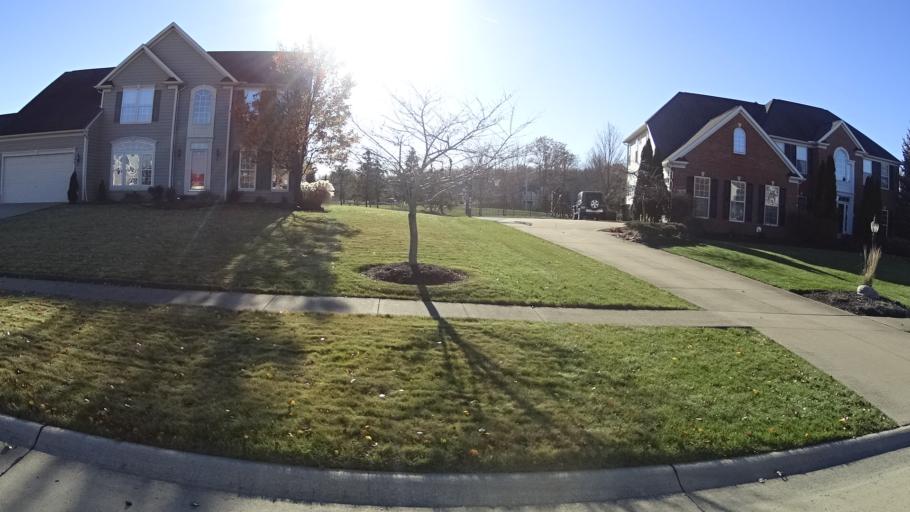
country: US
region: Ohio
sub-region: Lorain County
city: Avon Center
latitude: 41.4385
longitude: -81.9884
